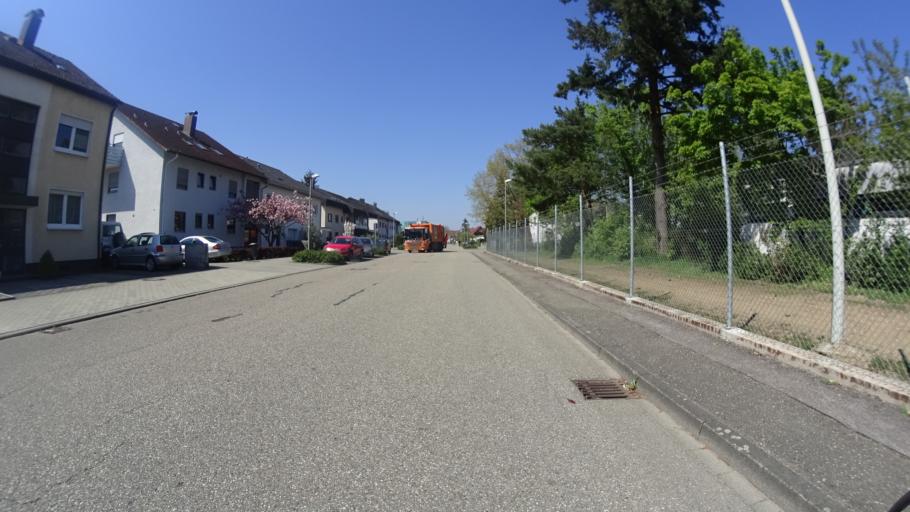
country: DE
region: Baden-Wuerttemberg
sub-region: Karlsruhe Region
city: Karlsruhe
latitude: 49.0439
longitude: 8.3966
